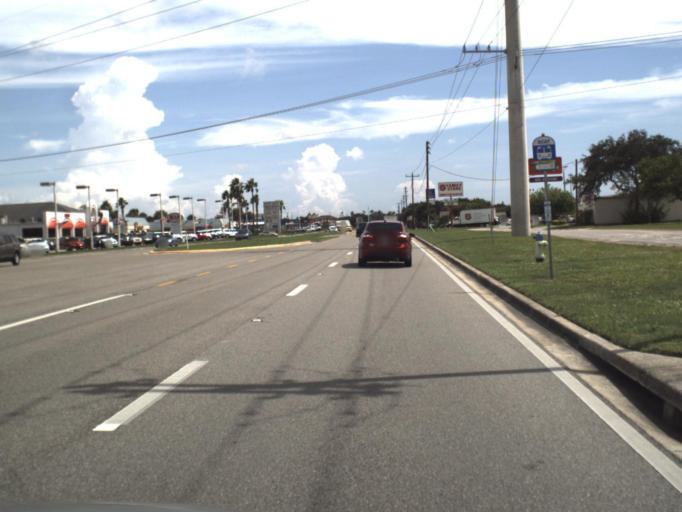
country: US
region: Florida
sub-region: Sarasota County
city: Venice Gardens
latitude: 27.0867
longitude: -82.4292
